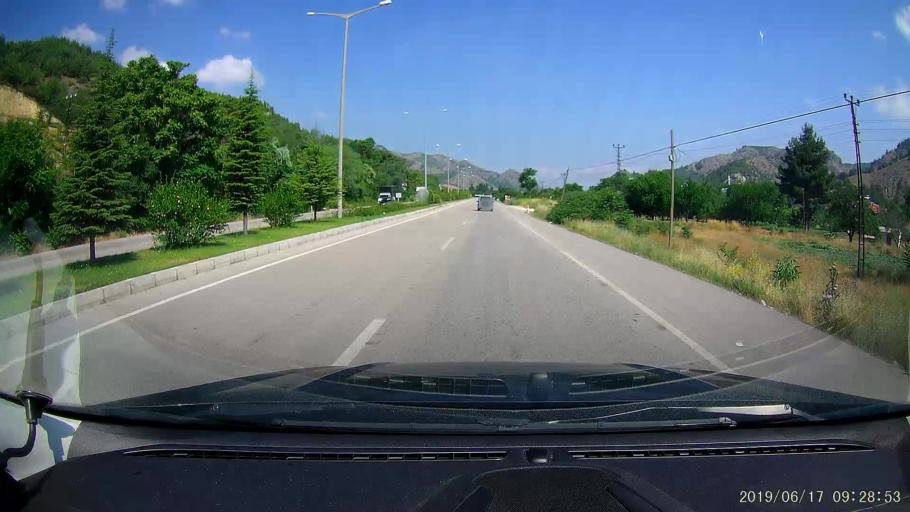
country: TR
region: Amasya
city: Amasya
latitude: 40.6930
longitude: 35.8191
